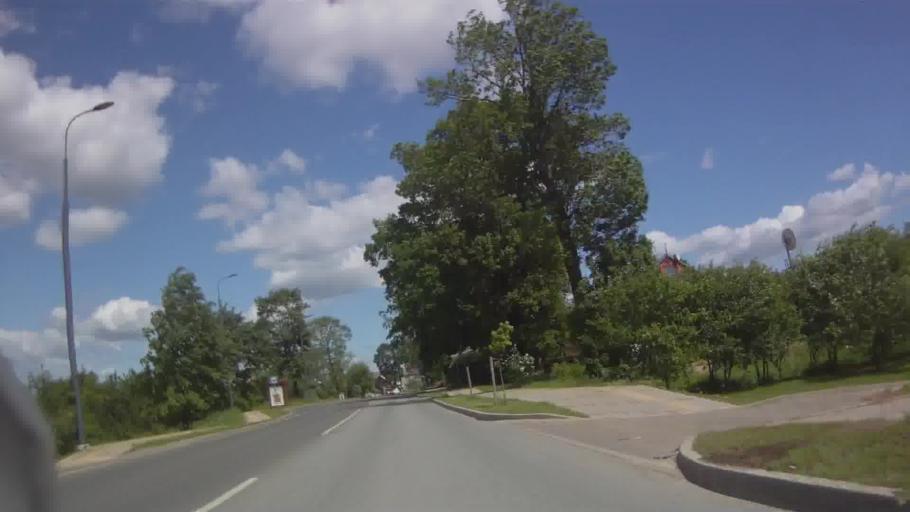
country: LV
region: Rezekne
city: Rezekne
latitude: 56.4938
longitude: 27.3190
